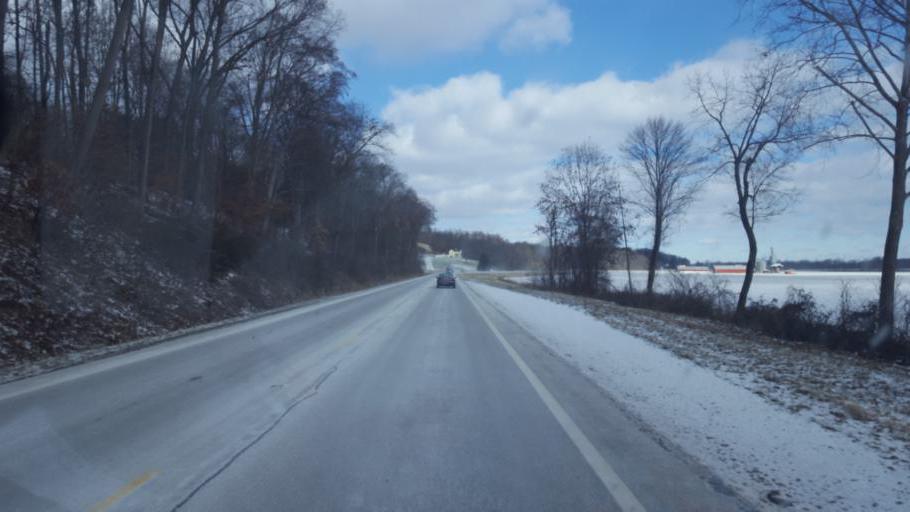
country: US
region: Ohio
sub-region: Coshocton County
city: Coshocton
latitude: 40.2265
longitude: -81.8814
